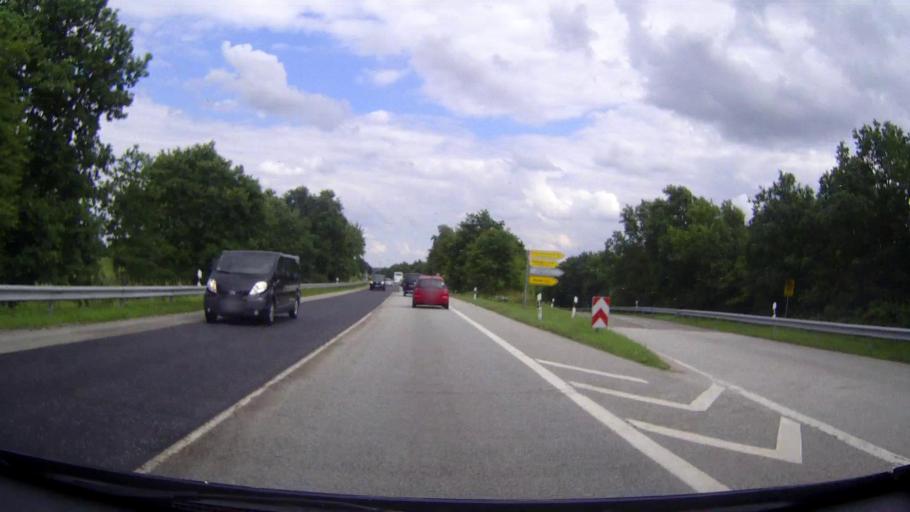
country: DE
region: Schleswig-Holstein
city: Klein Gladebrugge
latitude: 53.9233
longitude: 10.3309
